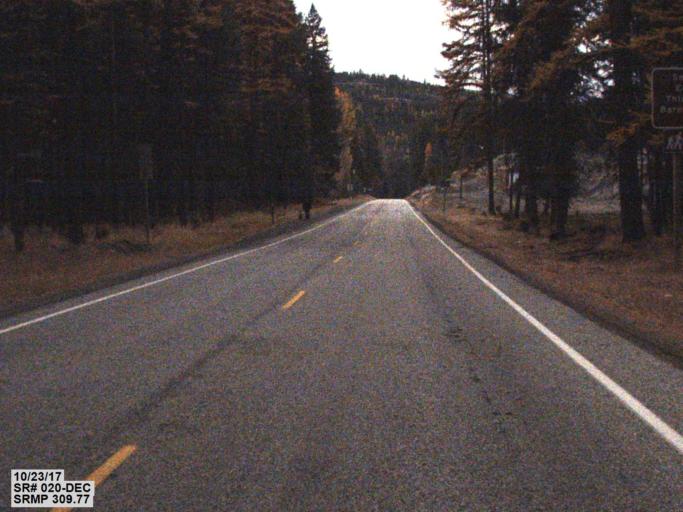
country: US
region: Washington
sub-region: Ferry County
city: Republic
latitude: 48.5969
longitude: -118.6408
